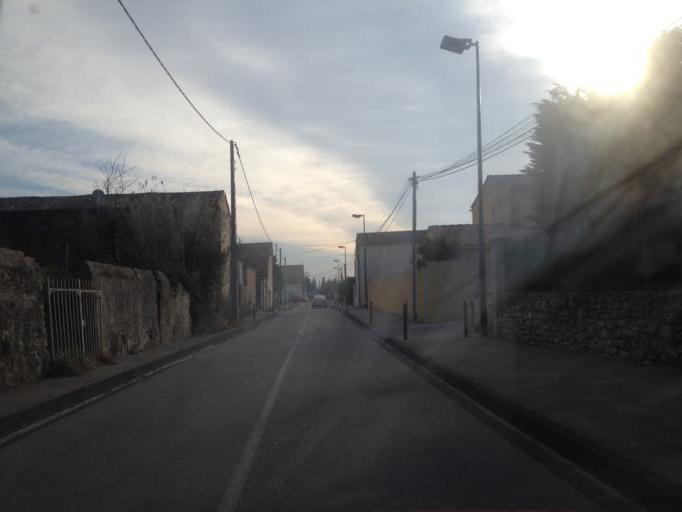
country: FR
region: Provence-Alpes-Cote d'Azur
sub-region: Departement du Vaucluse
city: Orange
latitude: 44.1249
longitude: 4.8012
